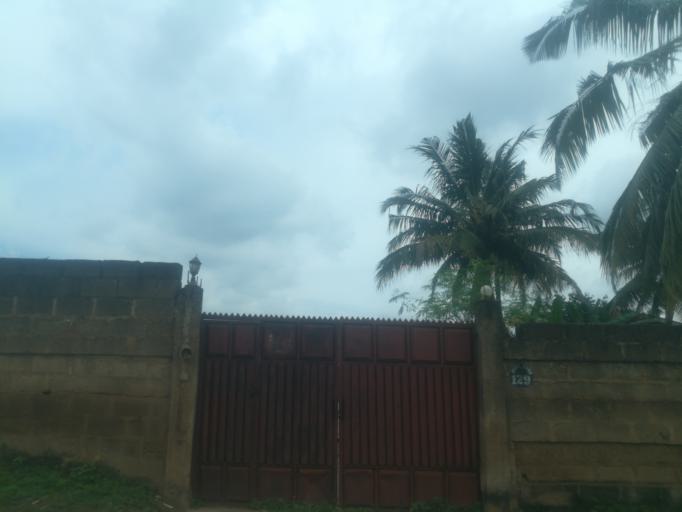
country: NG
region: Oyo
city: Ibadan
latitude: 7.3786
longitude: 3.9623
